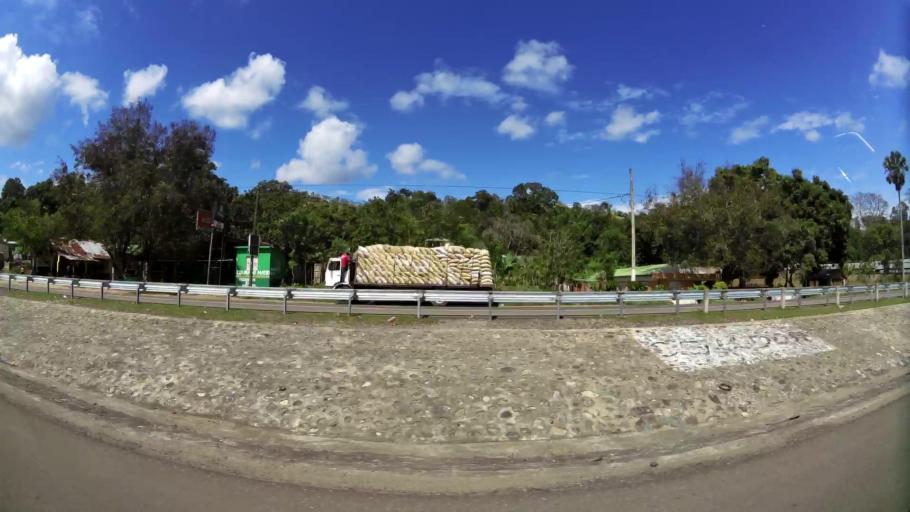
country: DO
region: La Vega
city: Concepcion de La Vega
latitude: 19.2571
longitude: -70.5675
